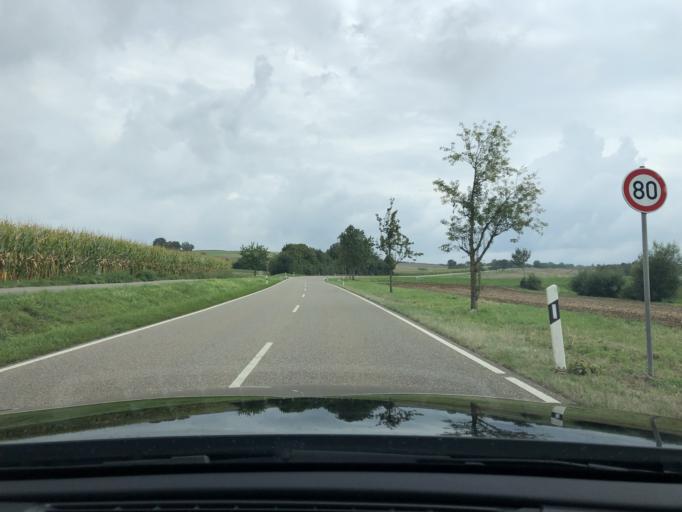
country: DE
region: Baden-Wuerttemberg
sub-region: Regierungsbezirk Stuttgart
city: Erdmannhausen
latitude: 48.9284
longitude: 9.2974
